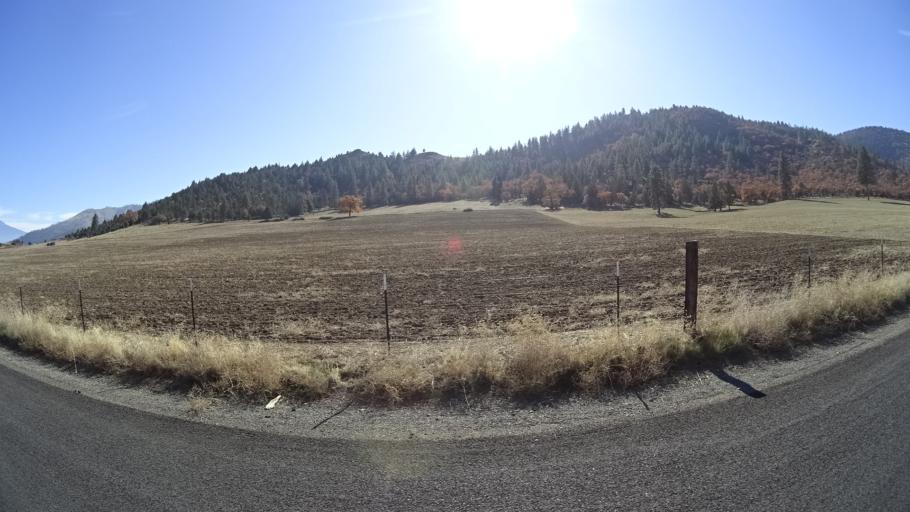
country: US
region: California
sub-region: Siskiyou County
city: Weed
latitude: 41.5028
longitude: -122.5669
